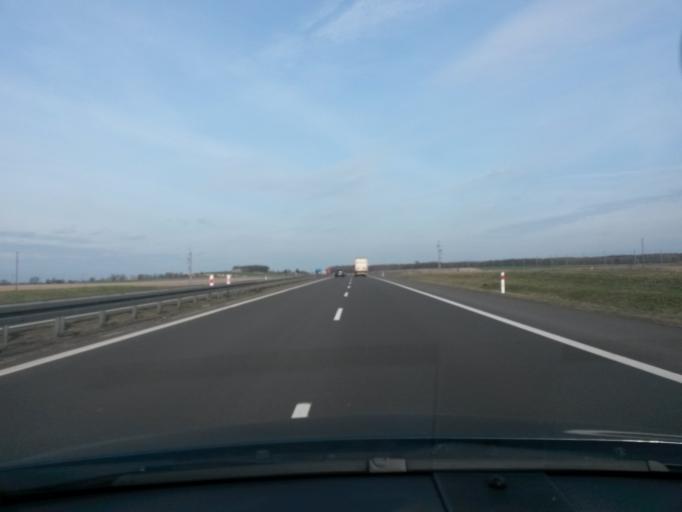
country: PL
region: Greater Poland Voivodeship
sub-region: Powiat sredzki
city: Dominowo
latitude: 52.3115
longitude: 17.3787
